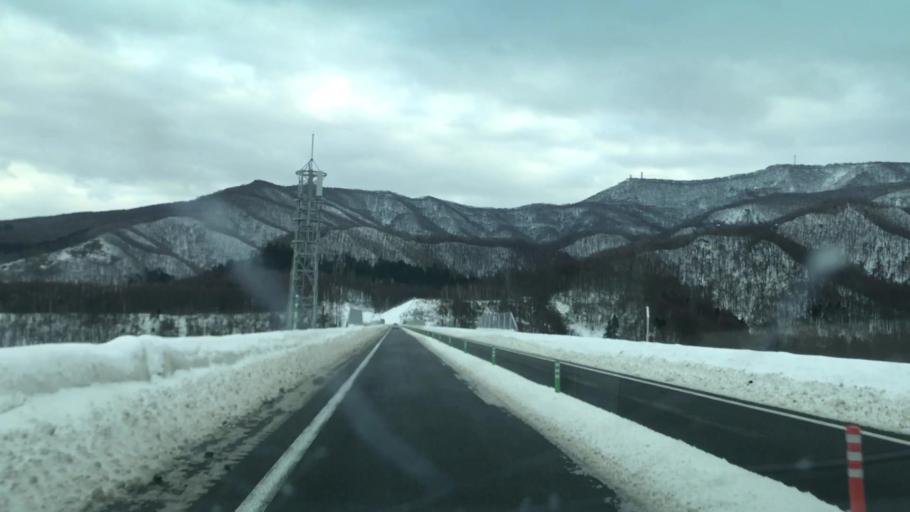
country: JP
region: Hokkaido
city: Otaru
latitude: 43.1668
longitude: 140.9851
